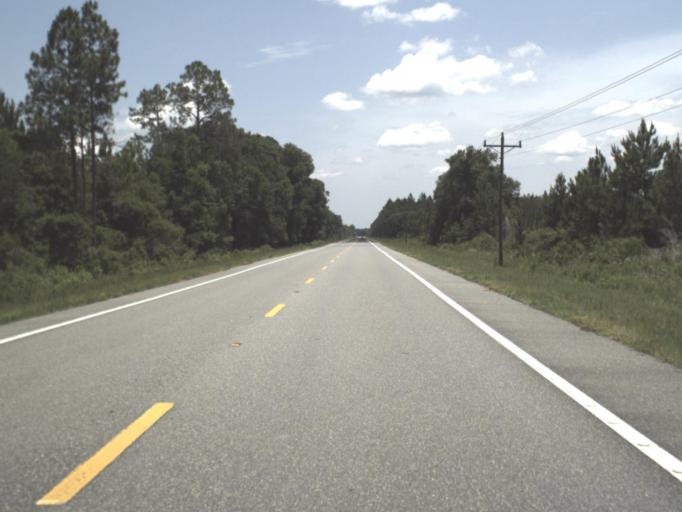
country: US
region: Florida
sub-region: Taylor County
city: Steinhatchee
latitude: 29.7668
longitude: -83.3398
